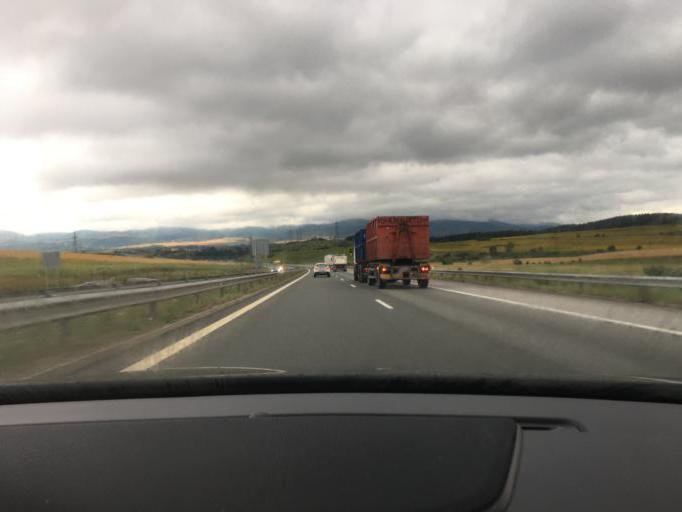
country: BG
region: Pernik
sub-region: Obshtina Pernik
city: Pernik
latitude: 42.6102
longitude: 23.1336
